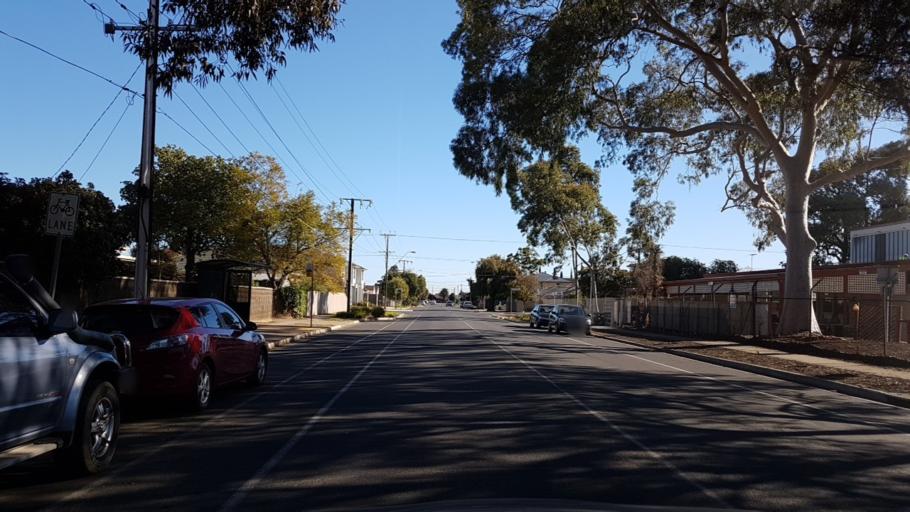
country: AU
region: South Australia
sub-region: City of West Torrens
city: Plympton
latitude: -34.9489
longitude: 138.5585
